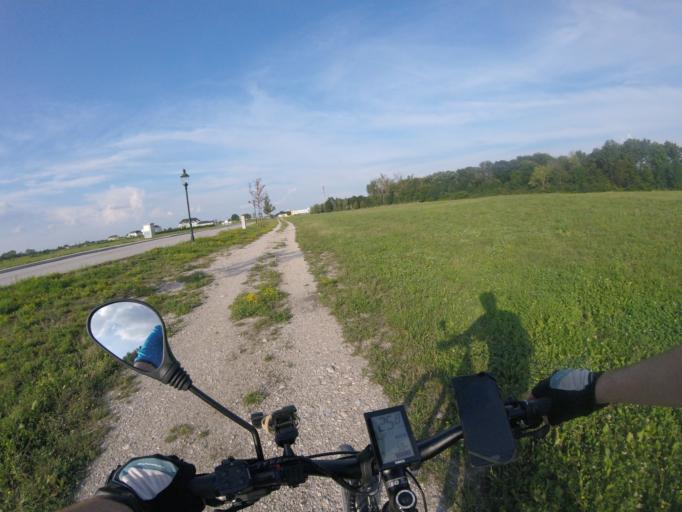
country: AT
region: Lower Austria
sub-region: Politischer Bezirk Baden
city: Ebreichsdorf
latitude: 47.9745
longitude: 16.3917
